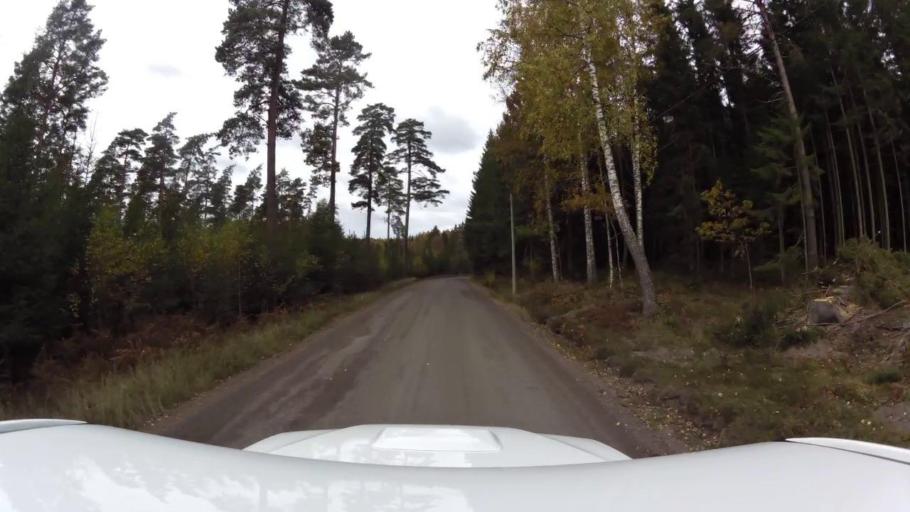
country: SE
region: OEstergoetland
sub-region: Linkopings Kommun
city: Berg
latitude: 58.5387
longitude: 15.5943
